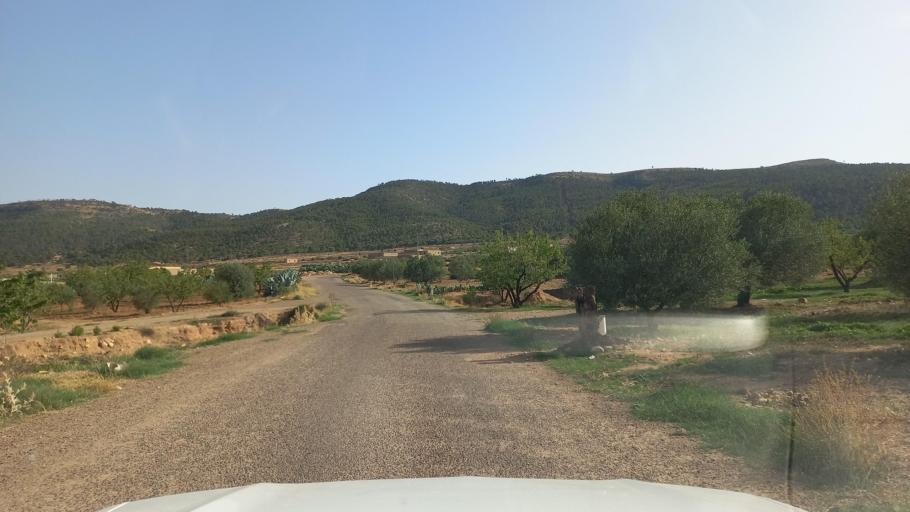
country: TN
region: Al Qasrayn
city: Kasserine
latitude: 35.3434
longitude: 8.8346
